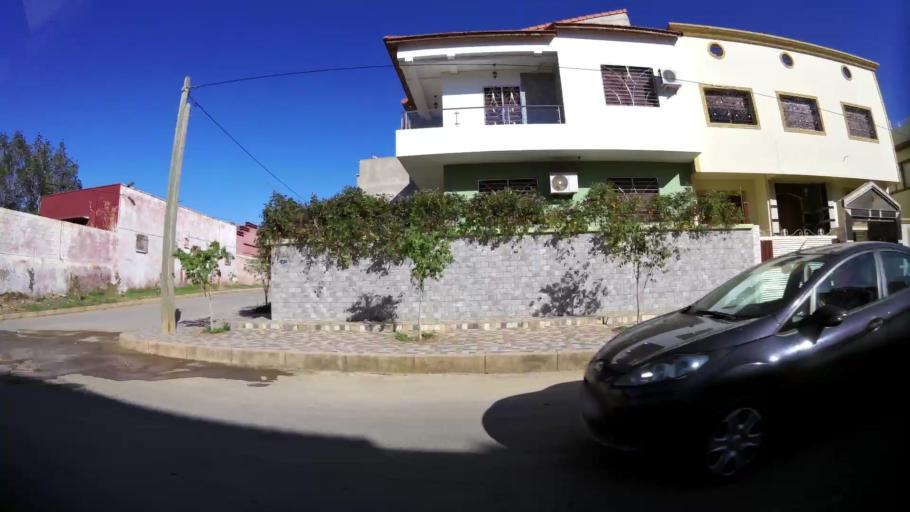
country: MA
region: Oriental
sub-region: Berkane-Taourirt
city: Berkane
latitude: 34.9321
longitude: -2.3286
